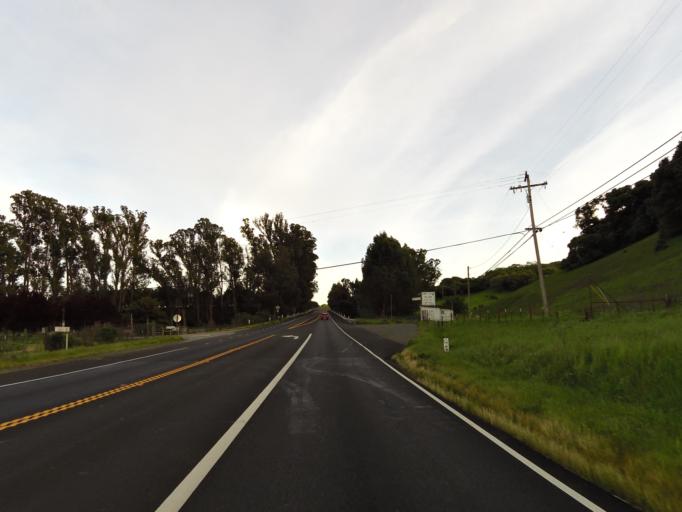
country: US
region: California
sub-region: Sonoma County
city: Temelec
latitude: 38.1916
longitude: -122.4436
